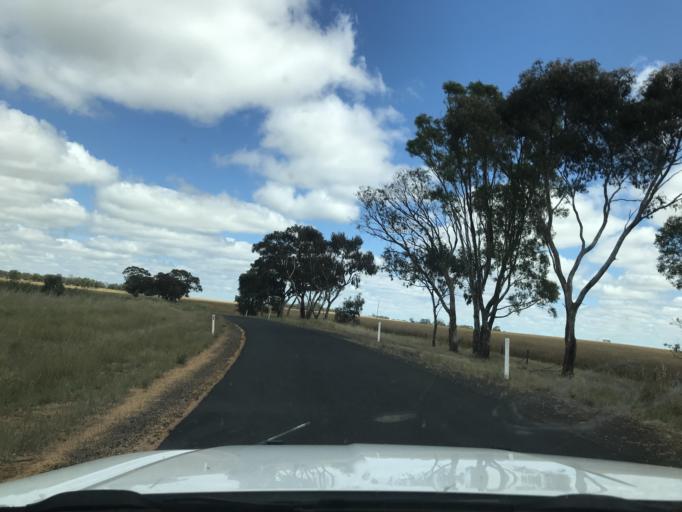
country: AU
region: South Australia
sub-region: Naracoorte and Lucindale
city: Naracoorte
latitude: -36.6844
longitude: 141.3216
